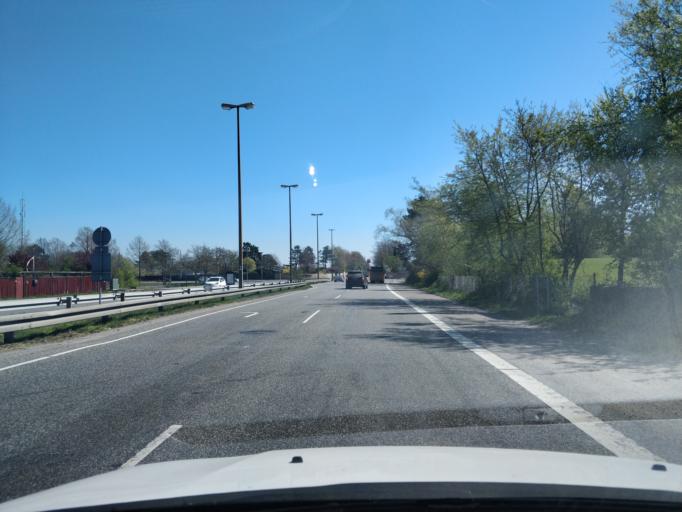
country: DK
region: Capital Region
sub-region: Ishoj Kommune
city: Ishoj
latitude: 55.6132
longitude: 12.3636
